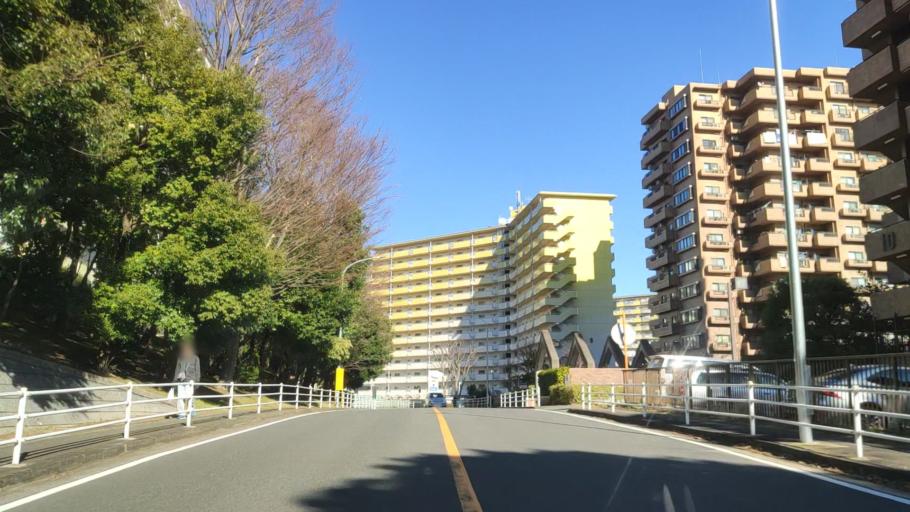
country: JP
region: Kanagawa
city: Minami-rinkan
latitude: 35.5037
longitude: 139.4965
